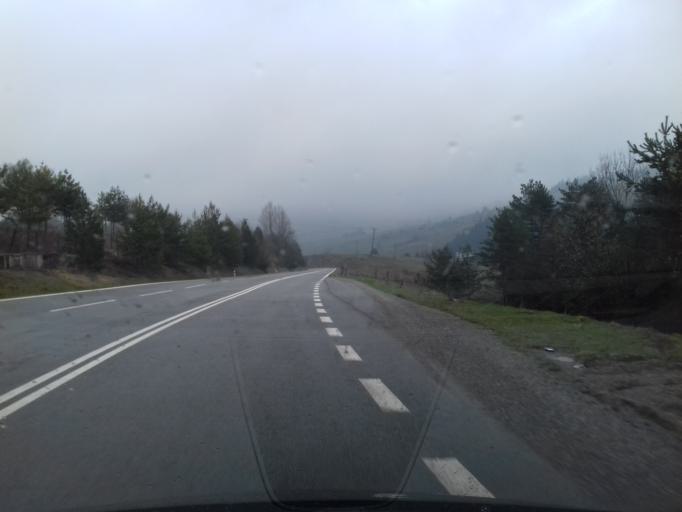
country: SK
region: Presovsky
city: Stara L'ubovna
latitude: 49.3545
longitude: 20.6788
